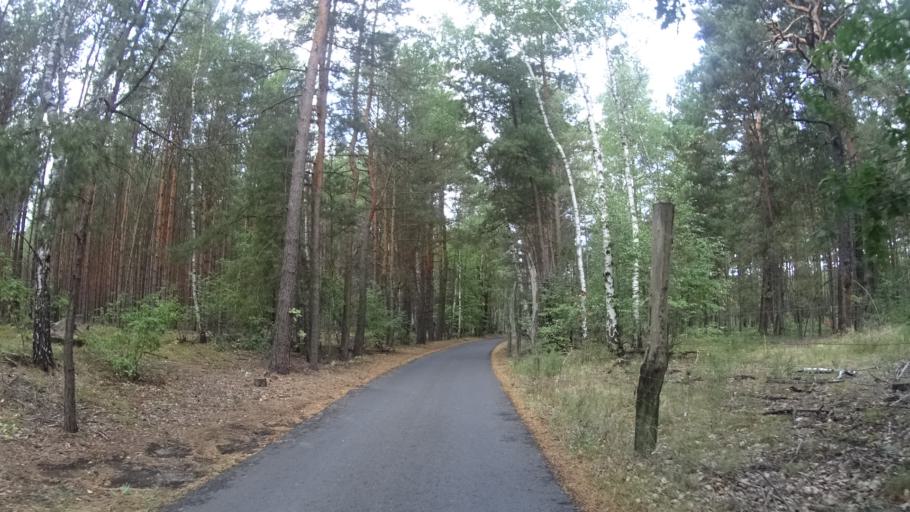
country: DE
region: Brandenburg
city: Tschernitz
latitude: 51.5859
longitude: 14.6033
